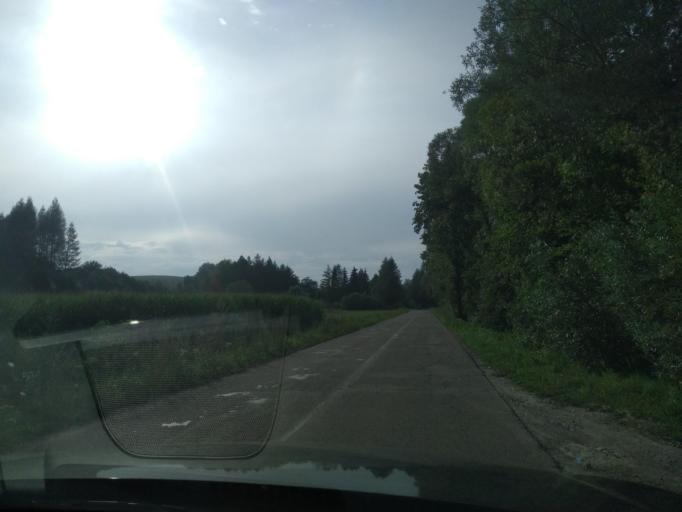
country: PL
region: Subcarpathian Voivodeship
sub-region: Powiat sanocki
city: Tyrawa Woloska
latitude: 49.5935
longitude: 22.3348
